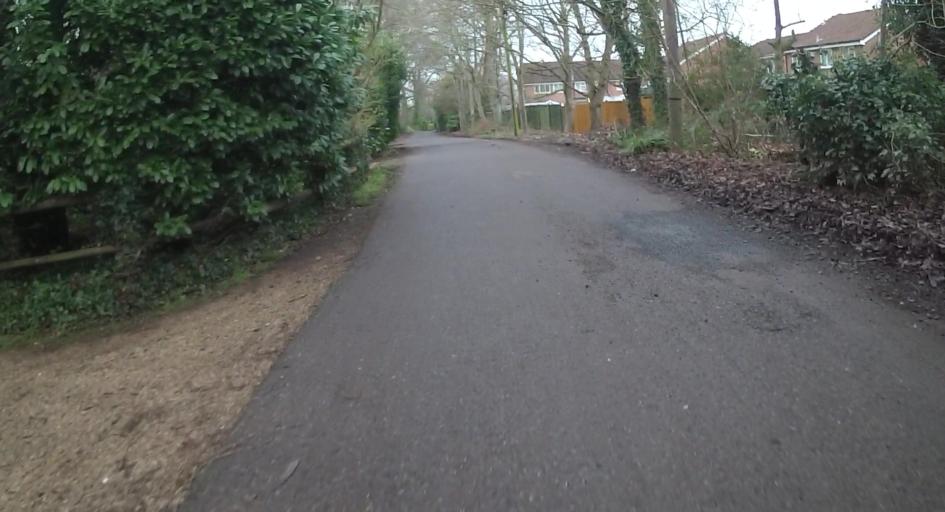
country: GB
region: England
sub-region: Wokingham
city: Barkham
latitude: 51.3888
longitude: -0.8597
